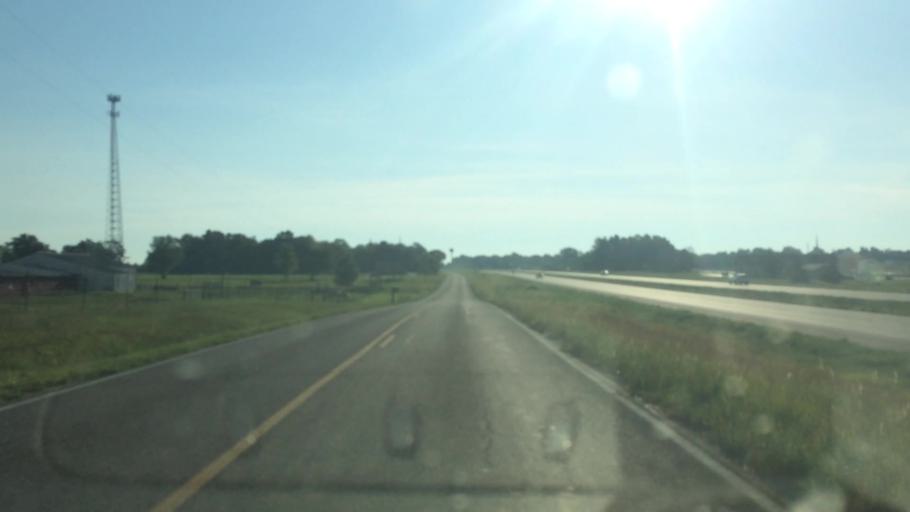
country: US
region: Missouri
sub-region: Greene County
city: Strafford
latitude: 37.2645
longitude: -93.1425
